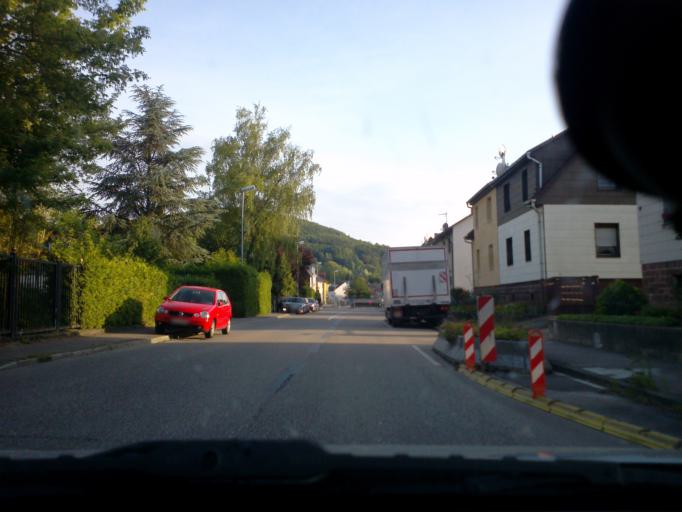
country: DE
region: Baden-Wuerttemberg
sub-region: Karlsruhe Region
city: Weingarten
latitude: 49.0082
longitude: 8.5312
